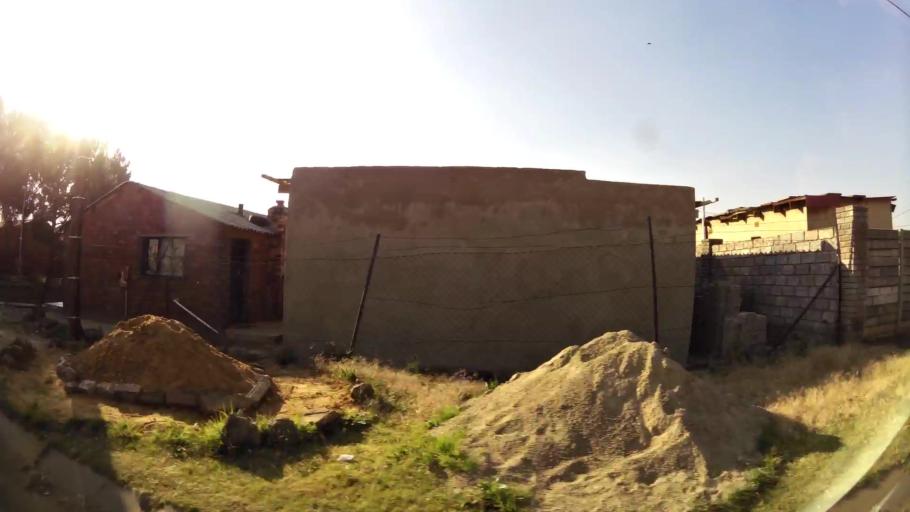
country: ZA
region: Gauteng
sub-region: City of Johannesburg Metropolitan Municipality
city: Soweto
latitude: -26.2674
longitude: 27.8682
